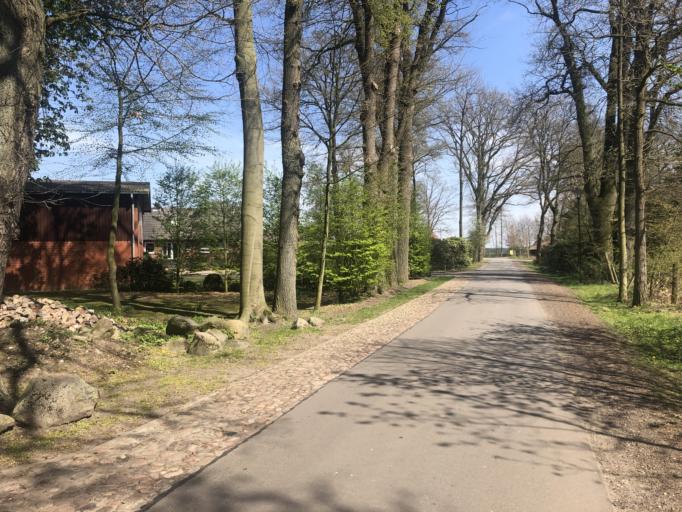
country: DE
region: Lower Saxony
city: Dotlingen
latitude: 52.9177
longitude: 8.3268
